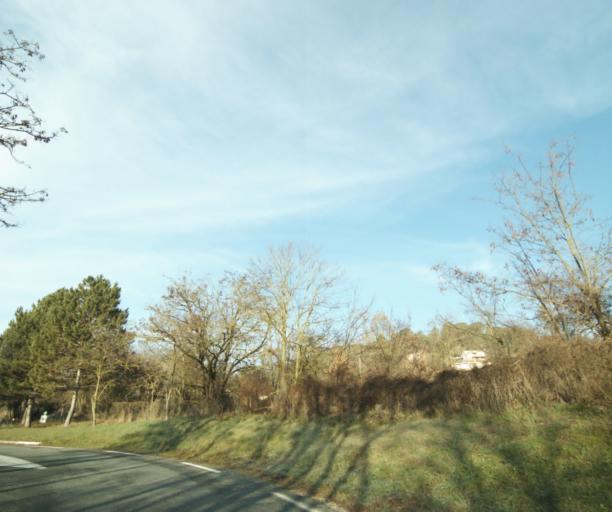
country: FR
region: Provence-Alpes-Cote d'Azur
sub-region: Departement du Var
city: Tourves
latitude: 43.4064
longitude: 5.9350
